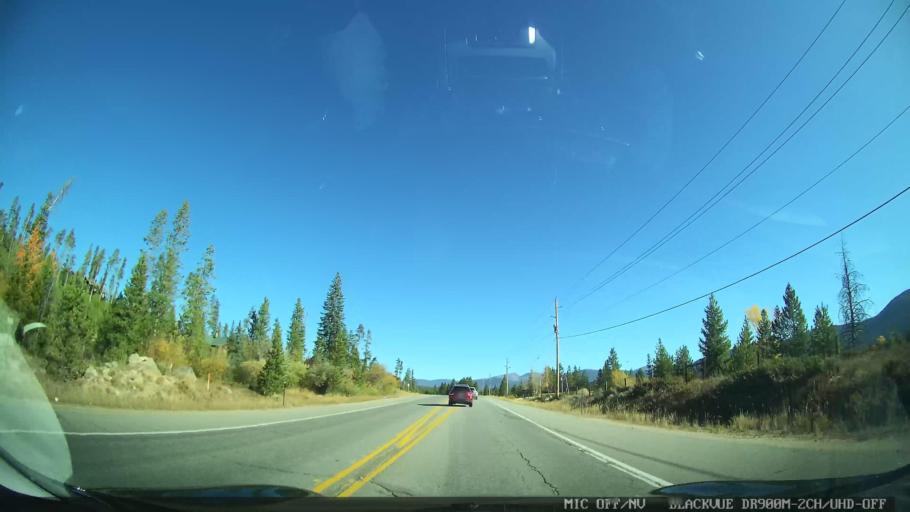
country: US
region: Colorado
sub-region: Grand County
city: Granby
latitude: 40.2047
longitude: -105.8610
